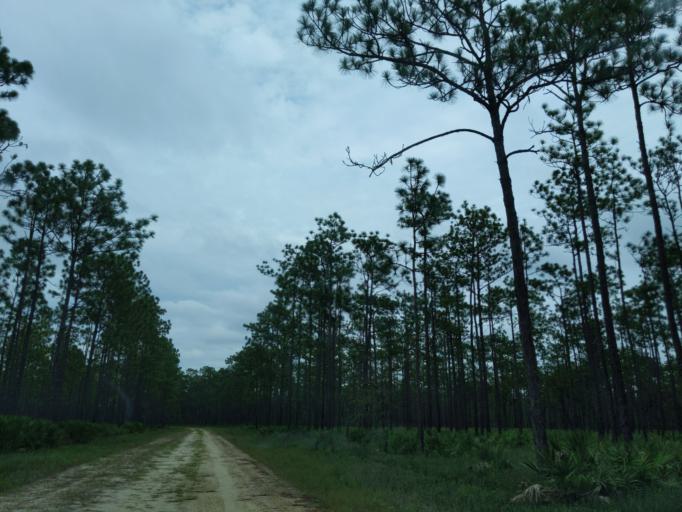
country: US
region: Florida
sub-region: Gadsden County
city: Midway
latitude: 30.3819
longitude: -84.4694
